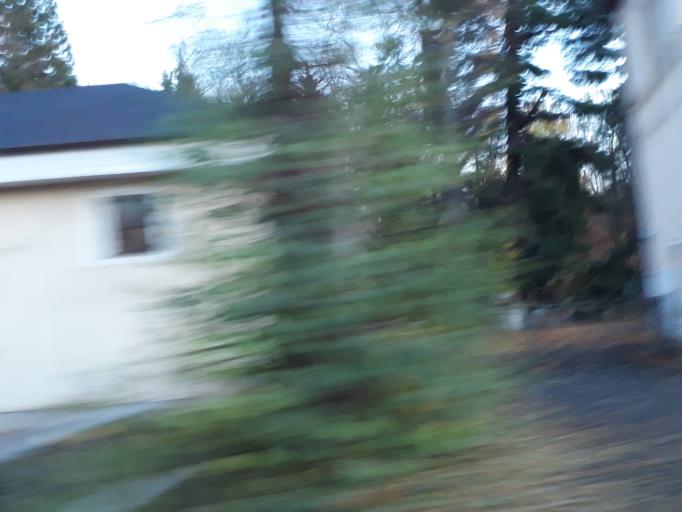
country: DE
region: Saxony
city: Kreischa
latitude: 50.9473
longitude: 13.7648
